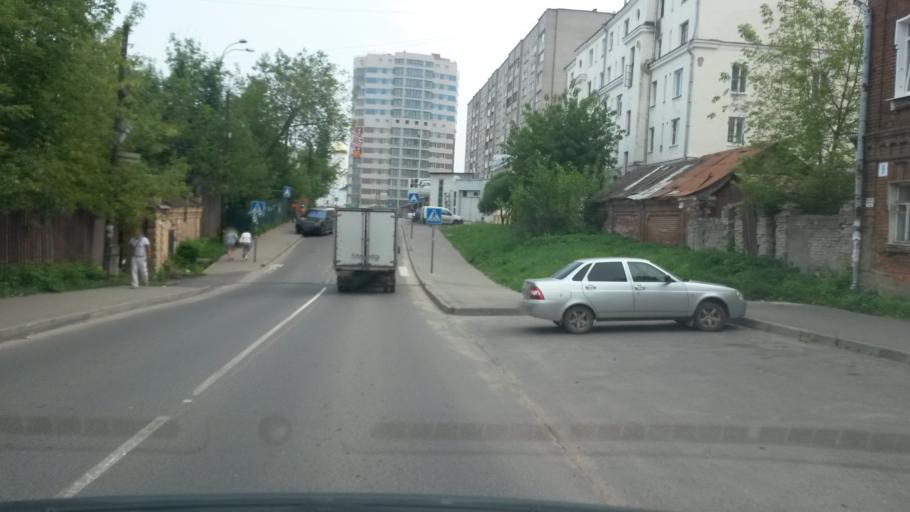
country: RU
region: Ivanovo
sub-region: Gorod Ivanovo
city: Ivanovo
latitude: 57.0009
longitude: 40.9688
